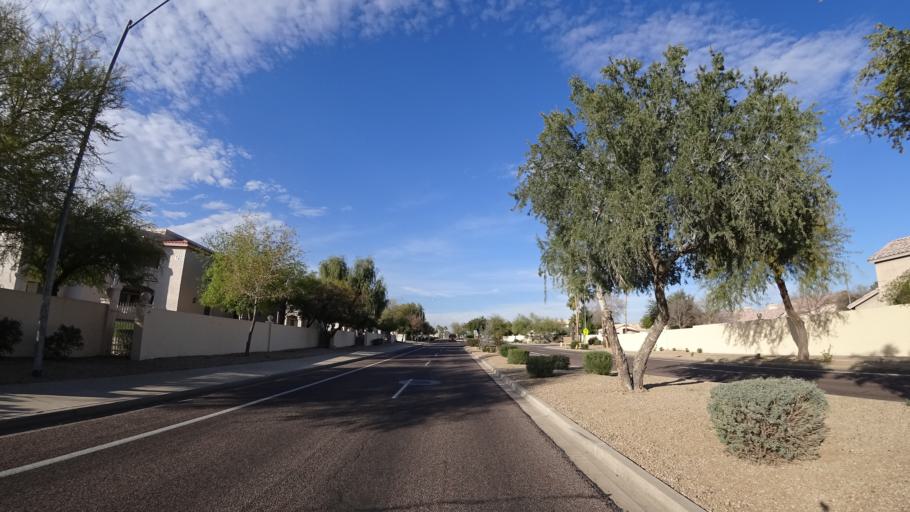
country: US
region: Arizona
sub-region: Maricopa County
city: Sun City
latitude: 33.6217
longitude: -112.2552
